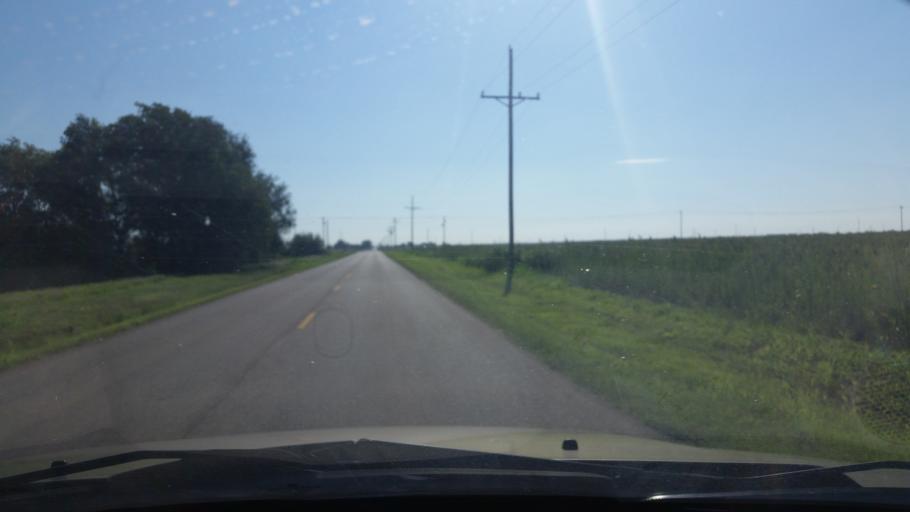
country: US
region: New Mexico
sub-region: Curry County
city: Clovis
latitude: 34.4338
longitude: -103.1636
